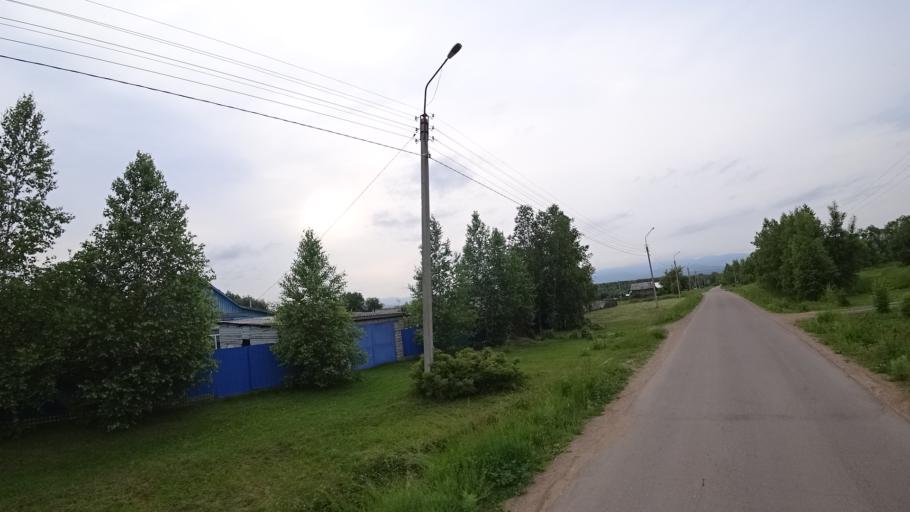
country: RU
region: Primorskiy
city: Novosysoyevka
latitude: 44.2343
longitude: 133.3594
